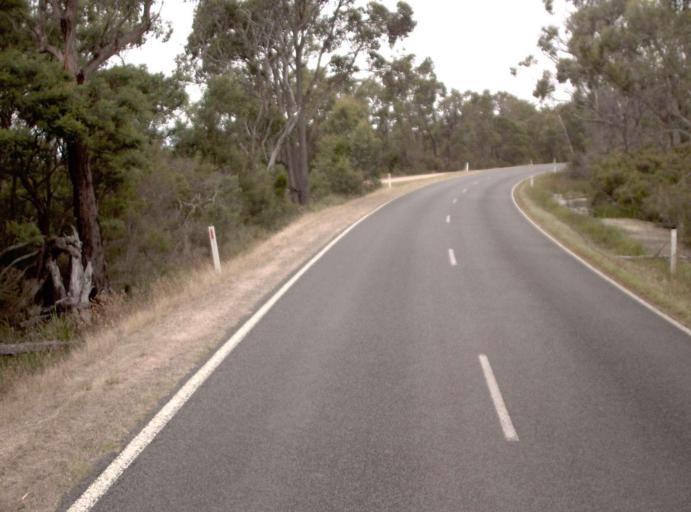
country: AU
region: Victoria
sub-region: Latrobe
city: Traralgon
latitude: -38.4983
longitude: 146.8340
